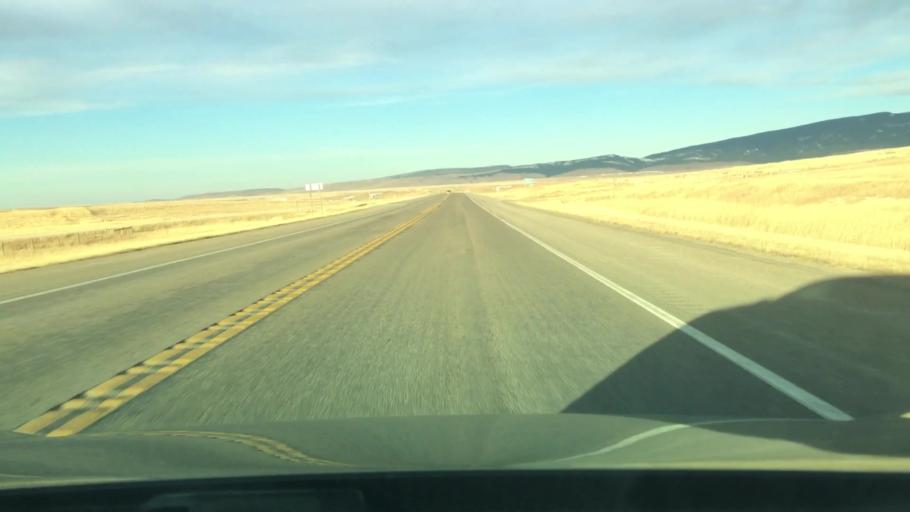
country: US
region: Montana
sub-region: Wheatland County
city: Harlowton
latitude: 46.6924
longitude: -109.7465
